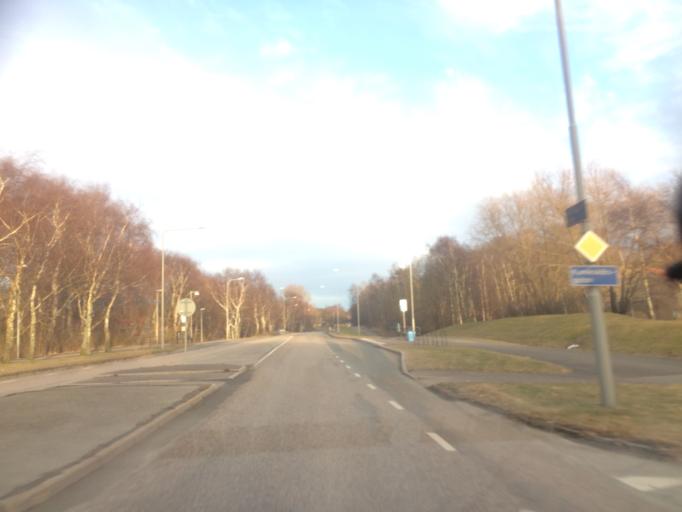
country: SE
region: Vaestra Goetaland
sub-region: Goteborg
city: Majorna
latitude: 57.6478
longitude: 11.8760
